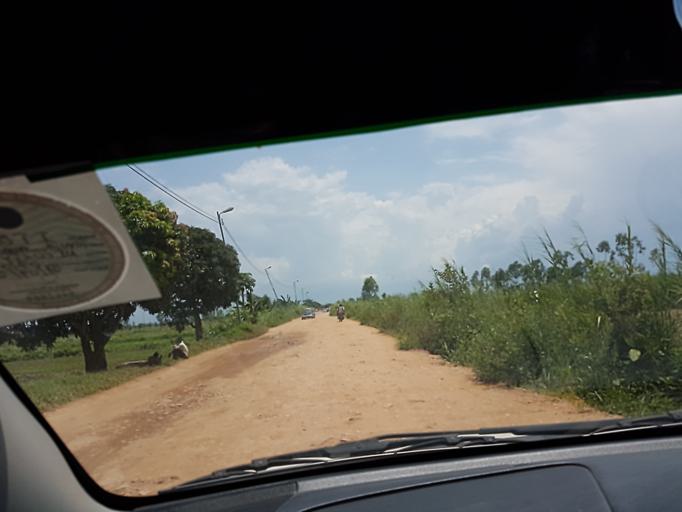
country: CD
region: South Kivu
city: Uvira
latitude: -3.3392
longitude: 29.2063
